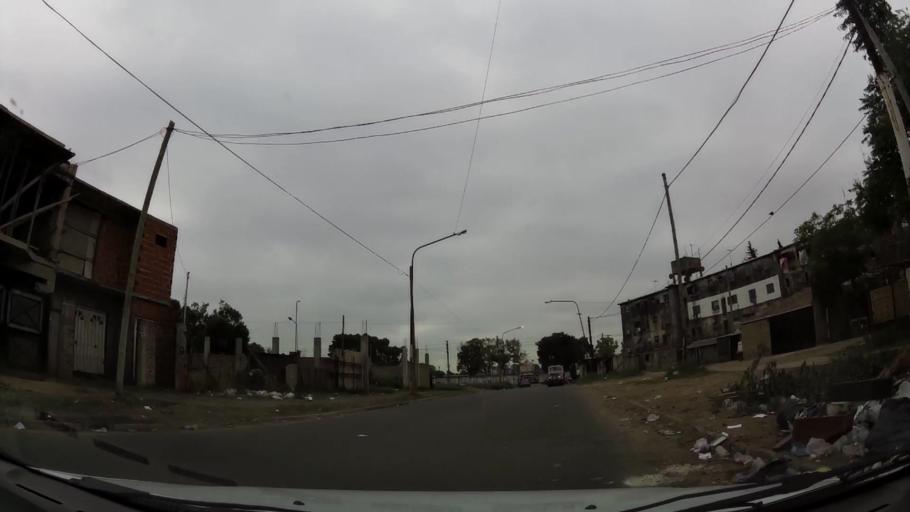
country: AR
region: Buenos Aires
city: San Justo
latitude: -34.7036
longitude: -58.5441
